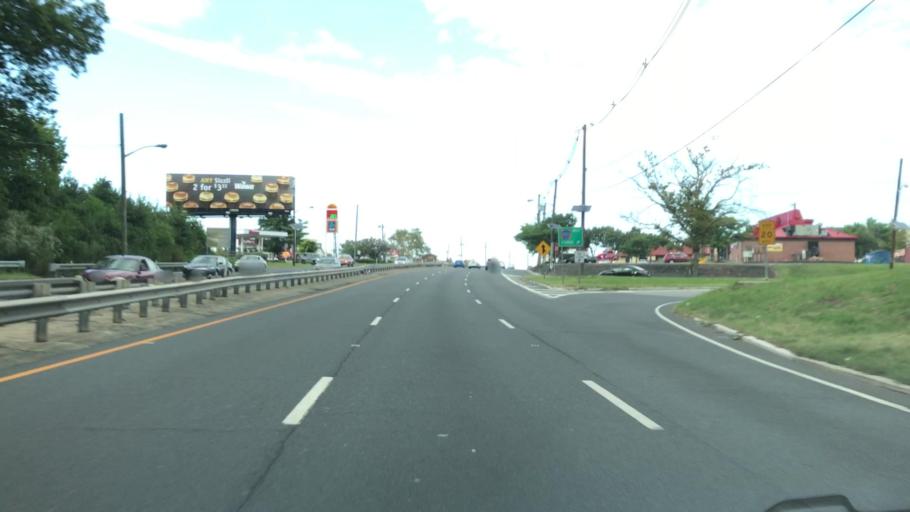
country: US
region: New Jersey
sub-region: Middlesex County
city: Fords
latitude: 40.5346
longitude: -74.2971
